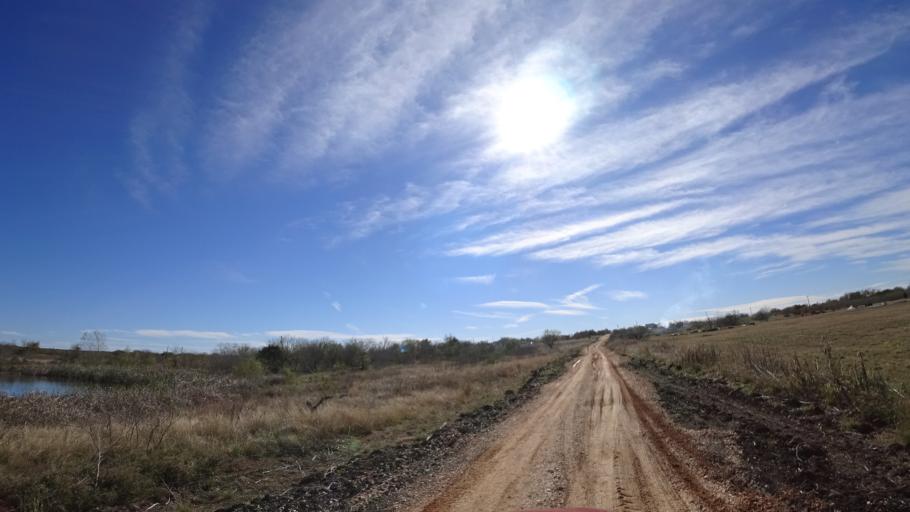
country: US
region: Texas
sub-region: Travis County
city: Onion Creek
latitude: 30.1106
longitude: -97.7157
